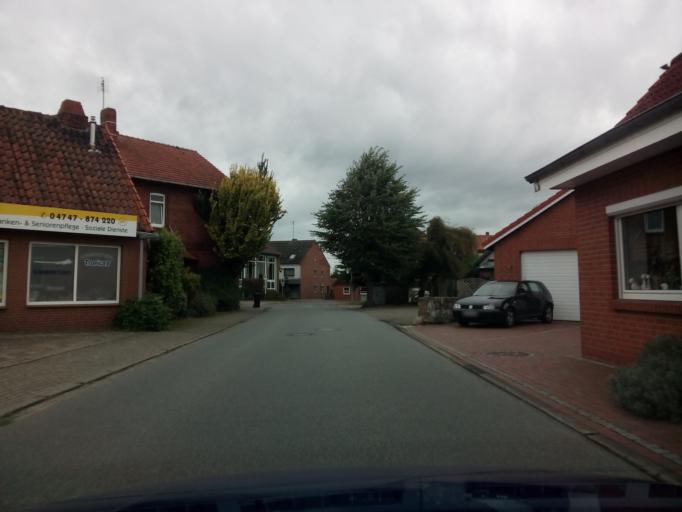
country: DE
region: Lower Saxony
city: Beverstedt
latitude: 53.4348
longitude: 8.8225
